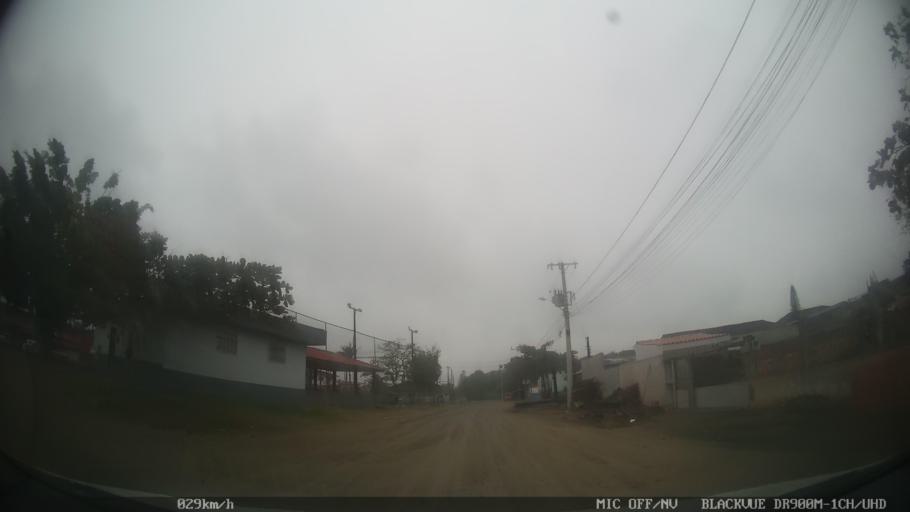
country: BR
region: Santa Catarina
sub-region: Joinville
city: Joinville
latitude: -26.2177
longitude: -48.8195
